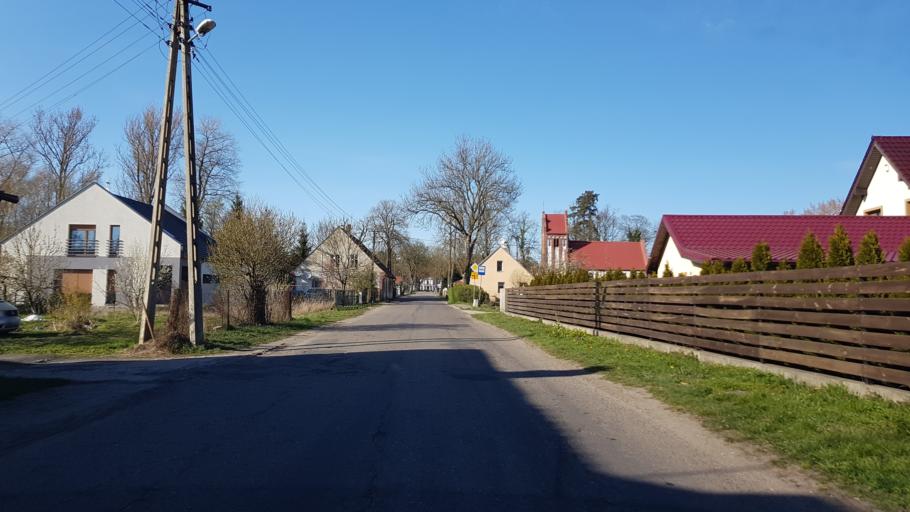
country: PL
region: West Pomeranian Voivodeship
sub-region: Powiat stargardzki
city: Stargard Szczecinski
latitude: 53.4031
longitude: 15.0290
